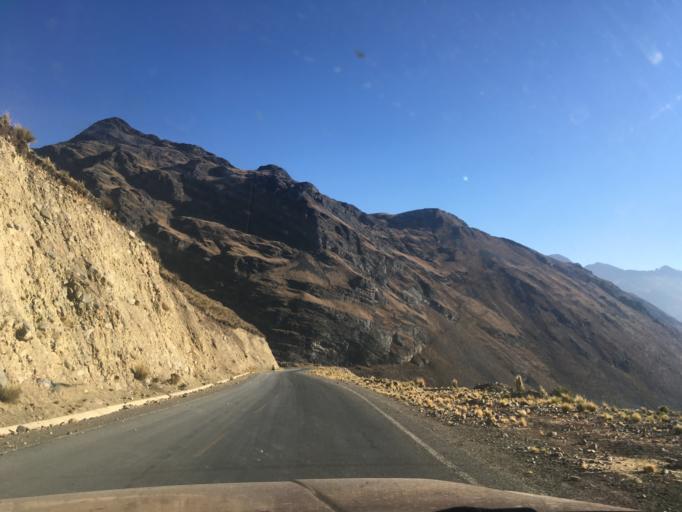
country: BO
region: La Paz
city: Quime
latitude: -17.0306
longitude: -67.2868
